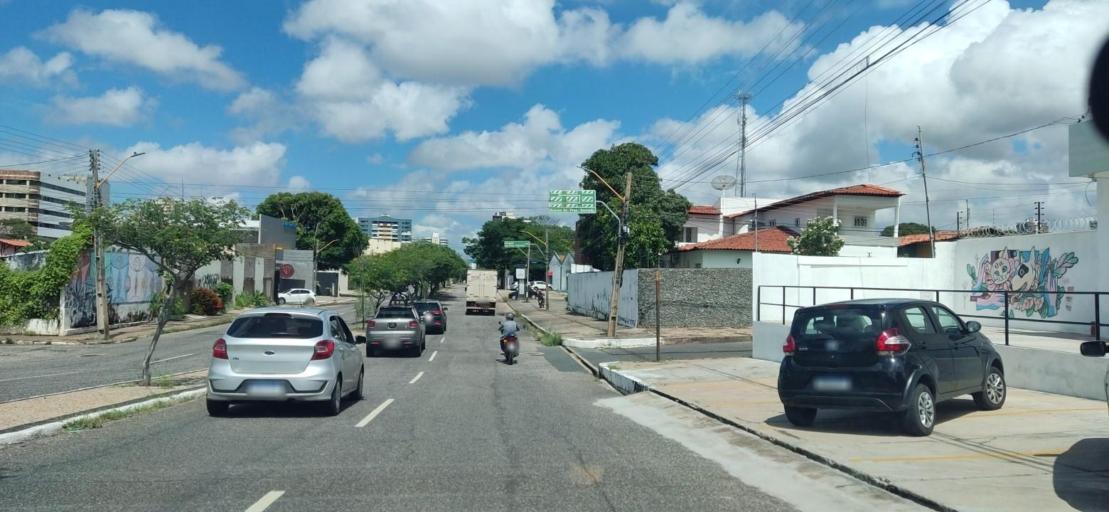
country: BR
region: Piaui
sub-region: Teresina
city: Teresina
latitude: -5.0706
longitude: -42.7683
